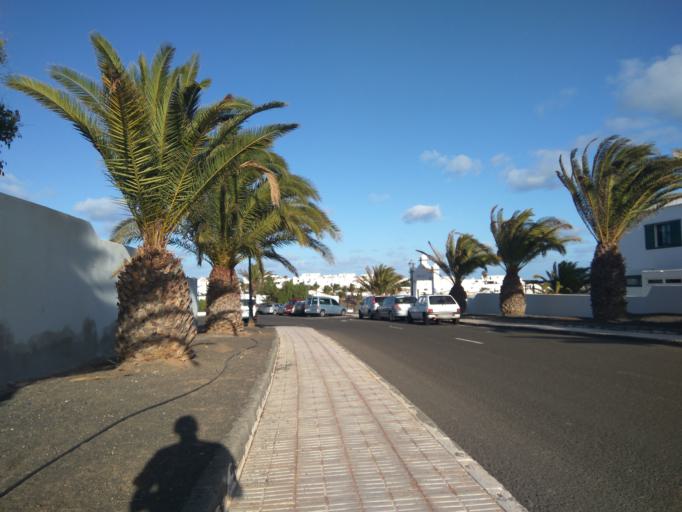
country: ES
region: Canary Islands
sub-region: Provincia de Las Palmas
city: Arrecife
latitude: 29.0059
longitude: -13.4881
